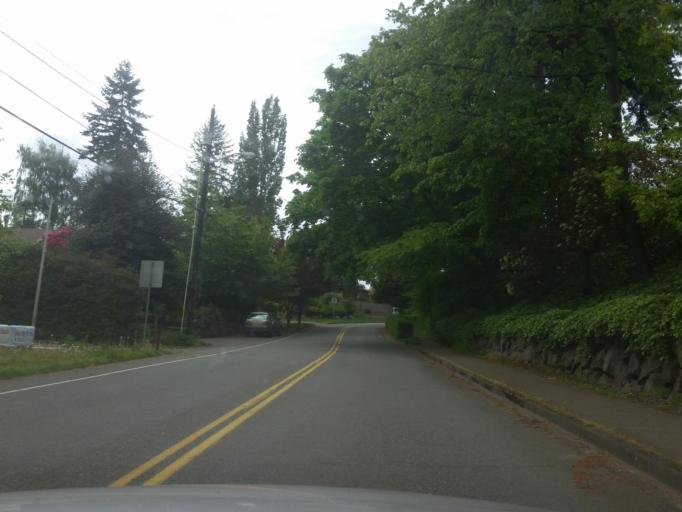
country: US
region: Washington
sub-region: King County
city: Kirkland
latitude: 47.6872
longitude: -122.2023
